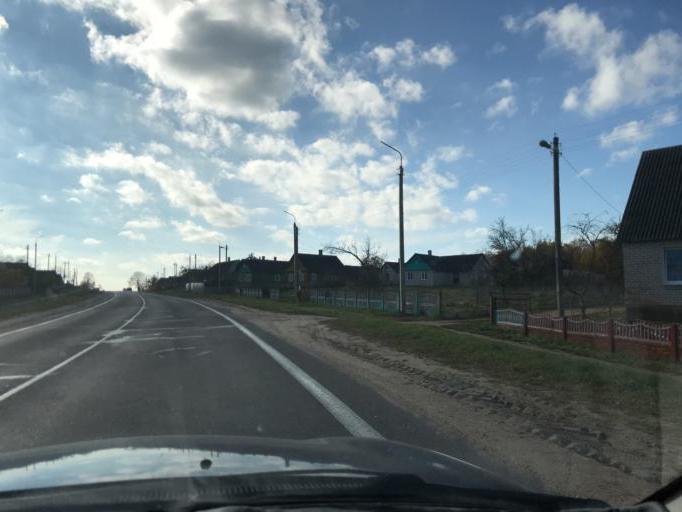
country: LT
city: Salcininkai
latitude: 54.2603
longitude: 25.3575
